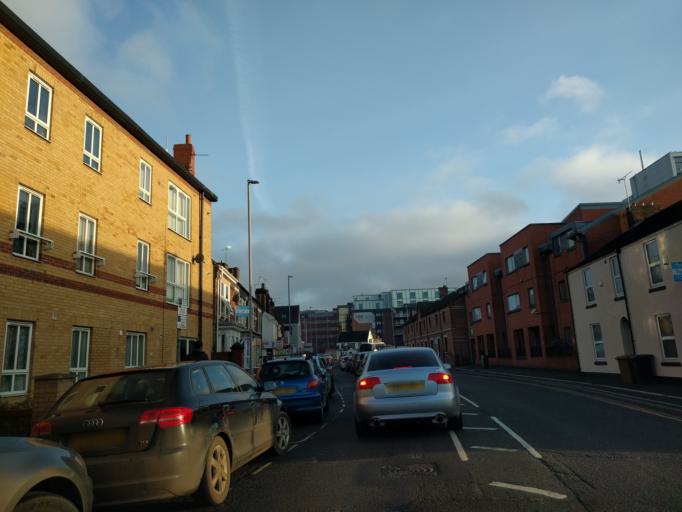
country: GB
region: England
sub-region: Lincolnshire
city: Lincoln
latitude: 53.2311
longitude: -0.5501
